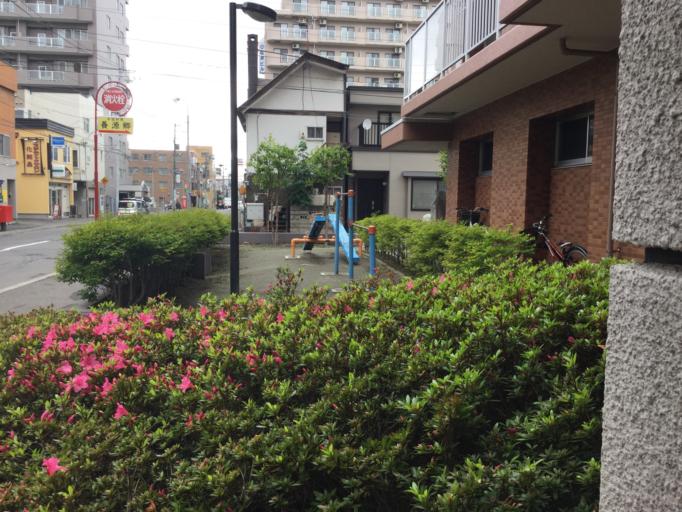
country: JP
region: Hokkaido
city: Sapporo
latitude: 43.0438
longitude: 141.3466
